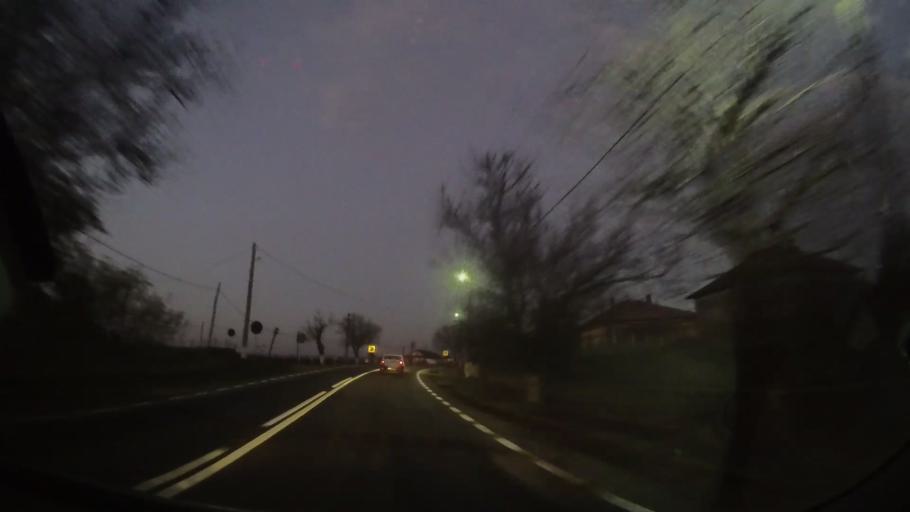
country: RO
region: Tulcea
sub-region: Comuna Frecatei
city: Cataloi
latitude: 45.1007
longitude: 28.7297
